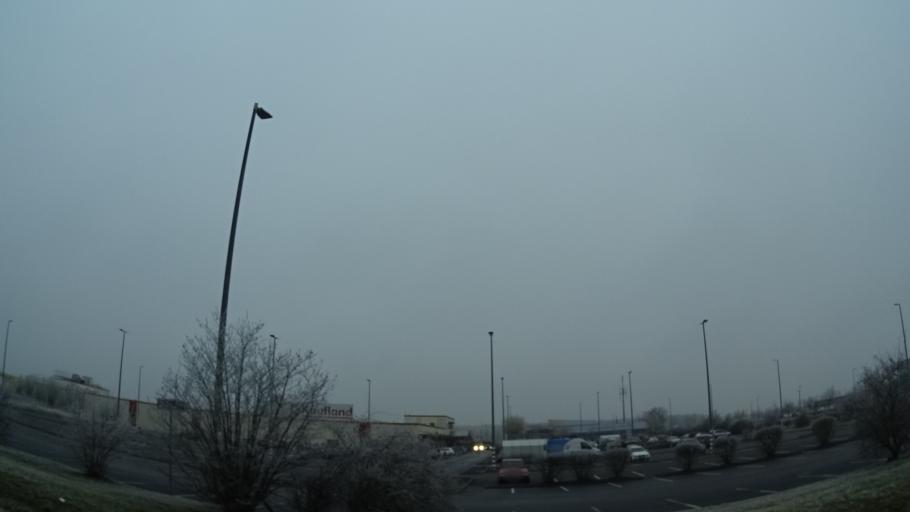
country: DE
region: Bavaria
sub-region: Regierungsbezirk Unterfranken
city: Albertshofen
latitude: 49.7550
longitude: 10.1785
